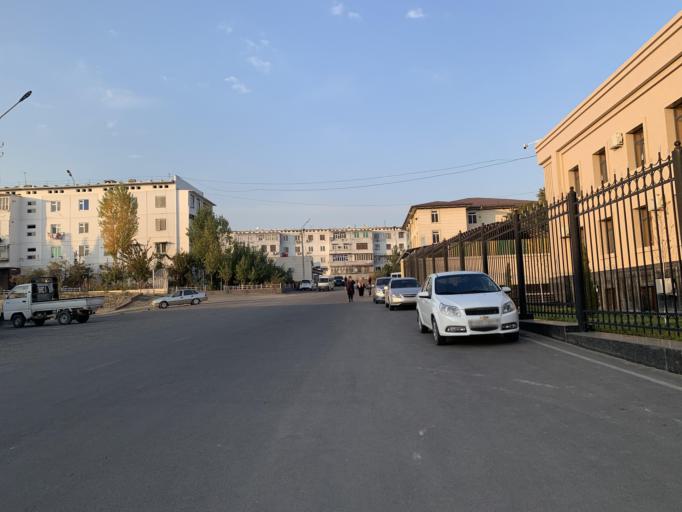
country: UZ
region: Namangan
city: Namangan Shahri
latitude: 41.0017
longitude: 71.6071
